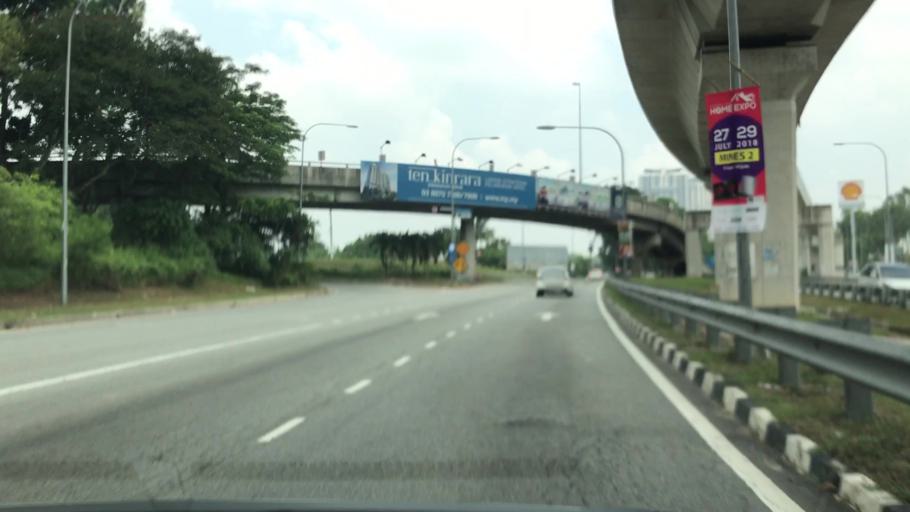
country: MY
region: Selangor
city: Subang Jaya
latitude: 3.0496
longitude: 101.6421
